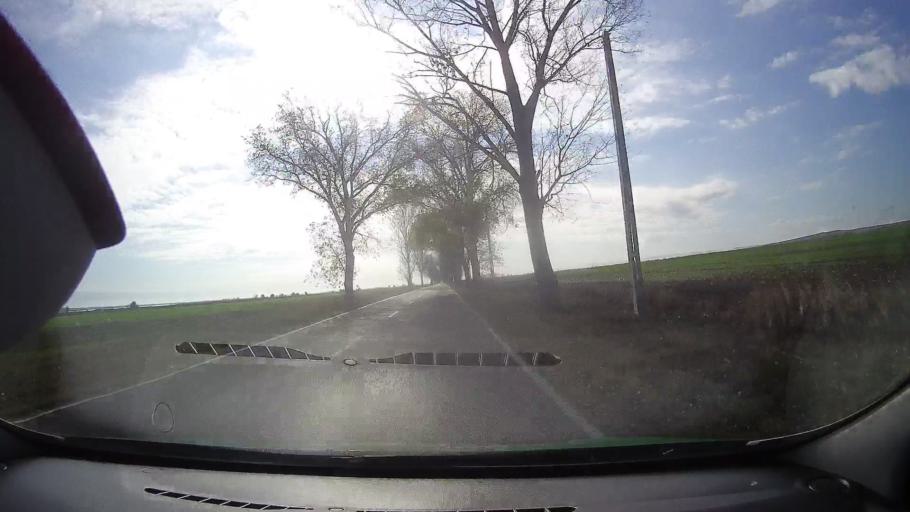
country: RO
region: Tulcea
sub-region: Comuna Valea Nucarilor
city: Agighiol
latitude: 45.0124
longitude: 28.8840
